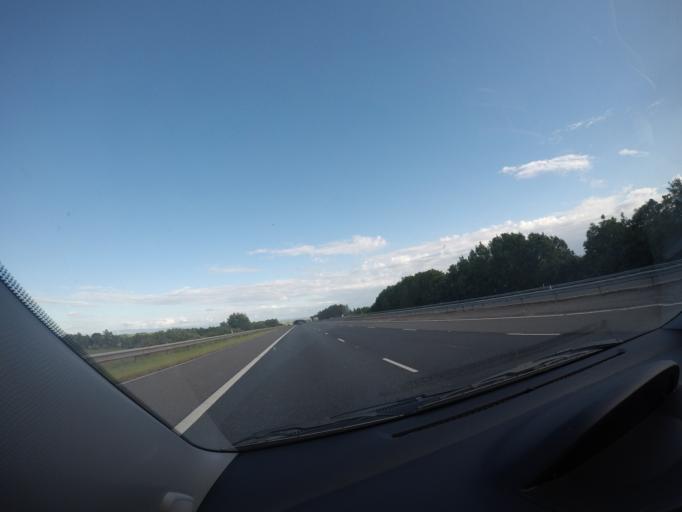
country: GB
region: Scotland
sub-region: Dumfries and Galloway
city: Gretna
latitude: 55.0220
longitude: -3.1239
